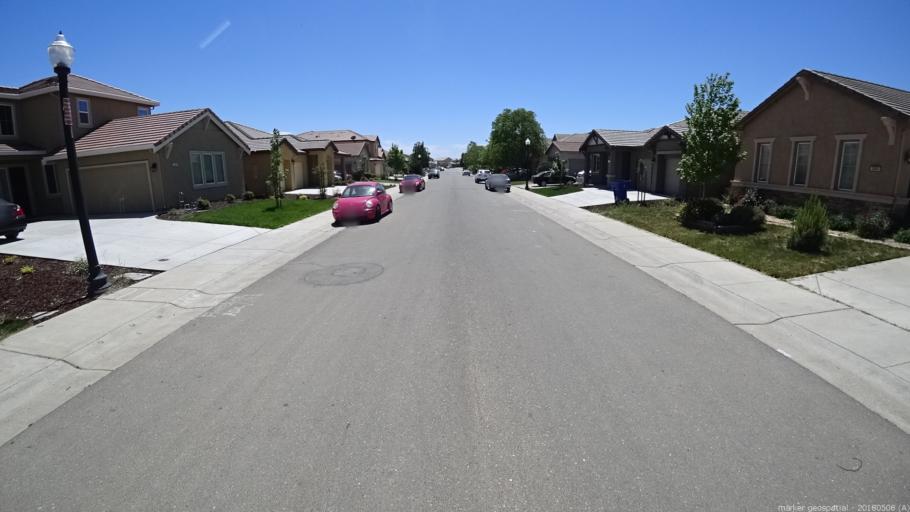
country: US
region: California
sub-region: Sacramento County
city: Elverta
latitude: 38.6836
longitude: -121.5307
